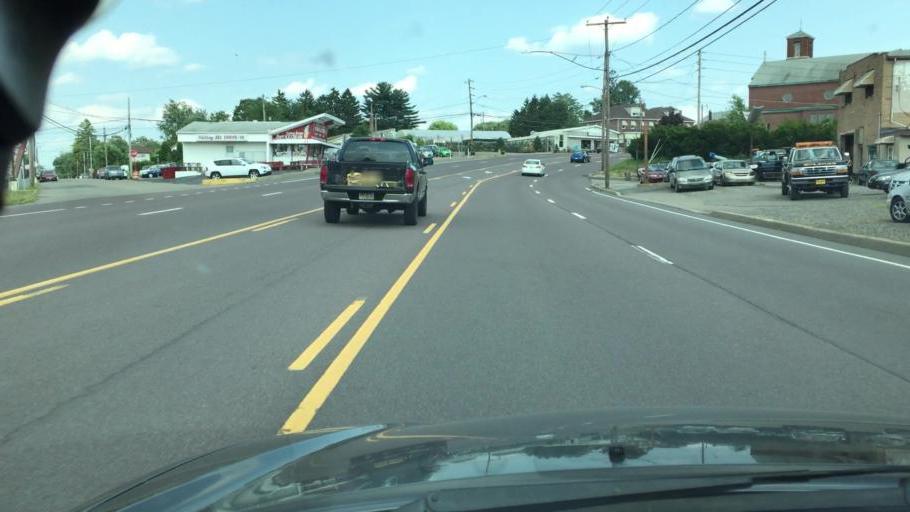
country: US
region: Pennsylvania
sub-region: Luzerne County
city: West Hazleton
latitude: 40.9658
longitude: -76.0005
